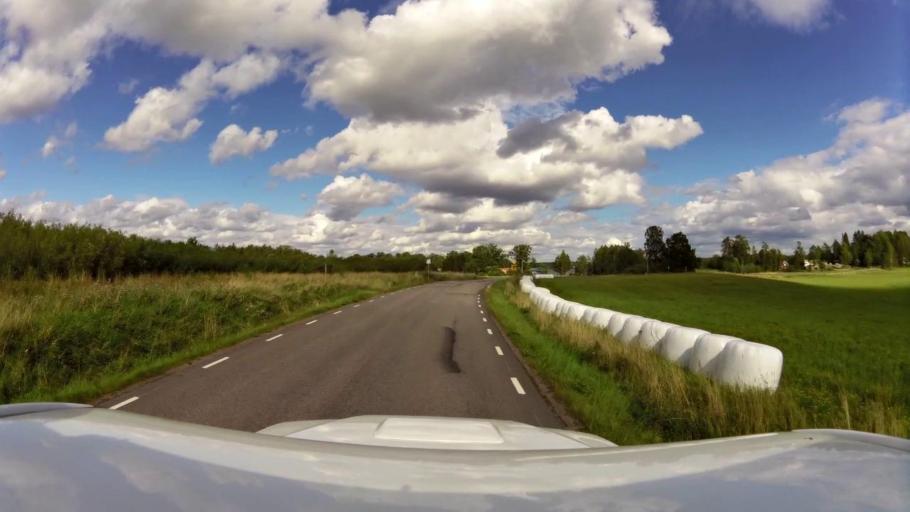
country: SE
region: OEstergoetland
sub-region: Kinda Kommun
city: Rimforsa
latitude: 58.2299
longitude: 15.6891
